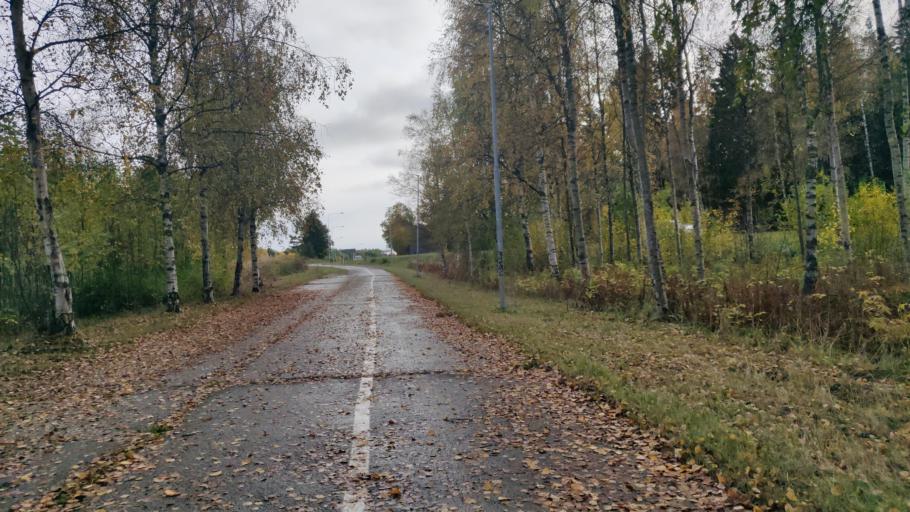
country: SE
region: Vaesternorrland
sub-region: Sundsvalls Kommun
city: Sundsbruk
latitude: 62.4321
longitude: 17.3426
